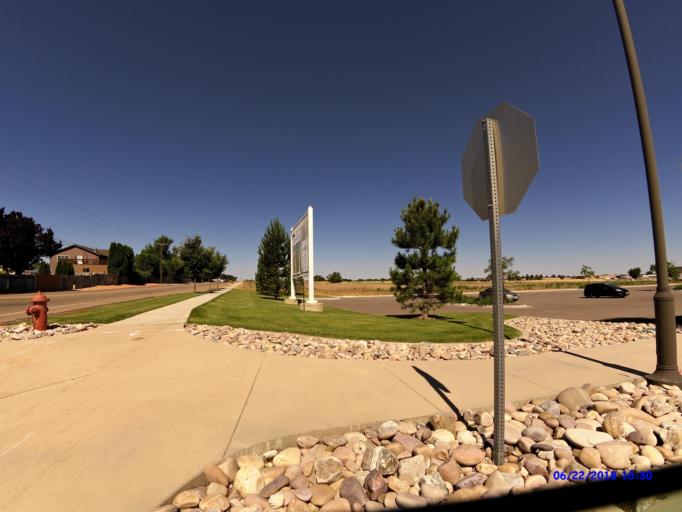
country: US
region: Utah
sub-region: Weber County
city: Riverdale
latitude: 41.1836
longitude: -112.0179
